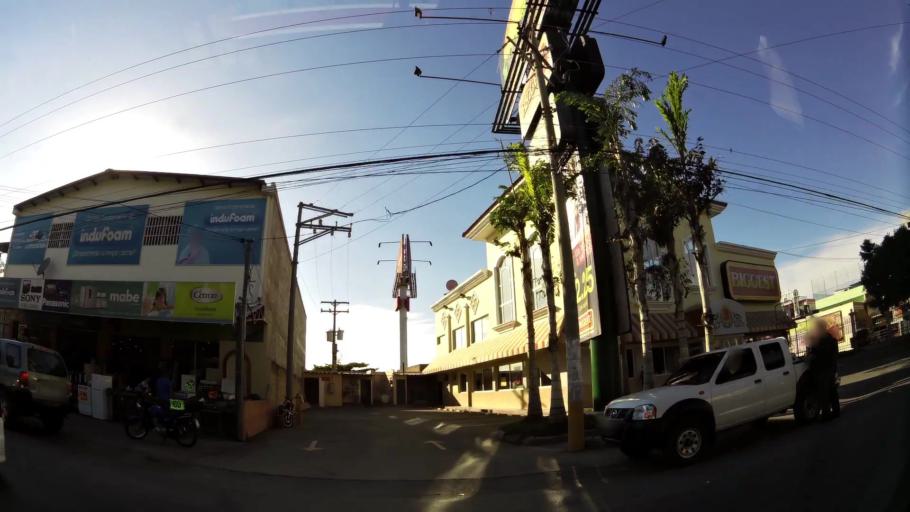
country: SV
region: Santa Ana
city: Metapan
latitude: 14.3304
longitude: -89.4424
